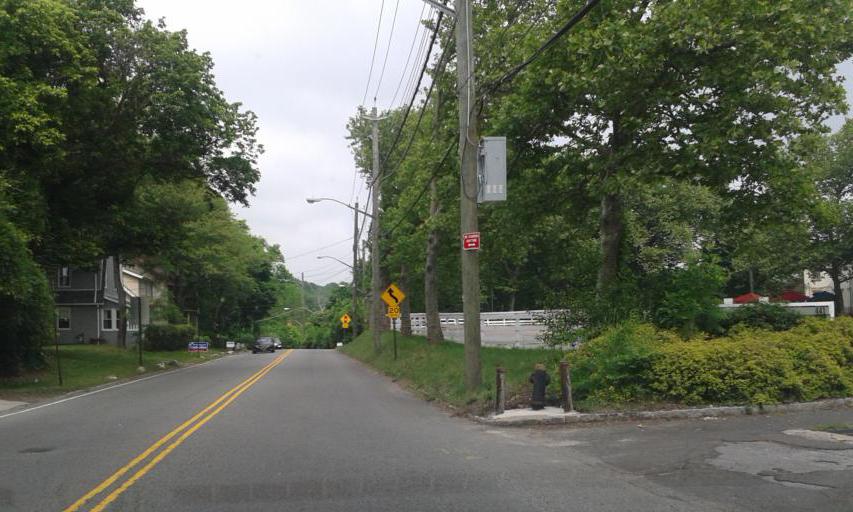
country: US
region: New York
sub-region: Richmond County
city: Staten Island
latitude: 40.5699
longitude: -74.1449
